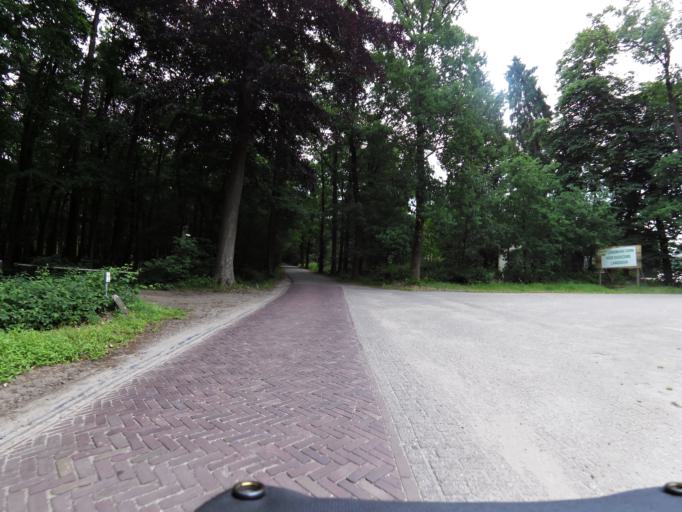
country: NL
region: North Brabant
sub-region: Gemeente Goirle
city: Goirle
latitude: 51.4836
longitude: 5.0849
